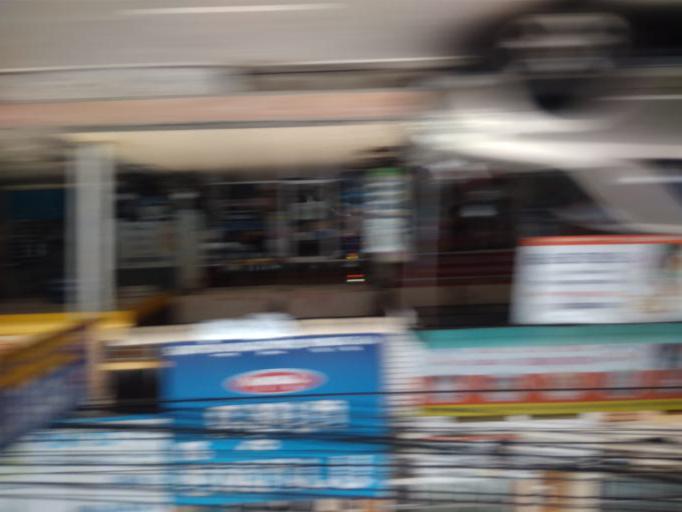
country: TH
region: Phuket
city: Ban Talat Nua
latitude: 7.8808
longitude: 98.3710
